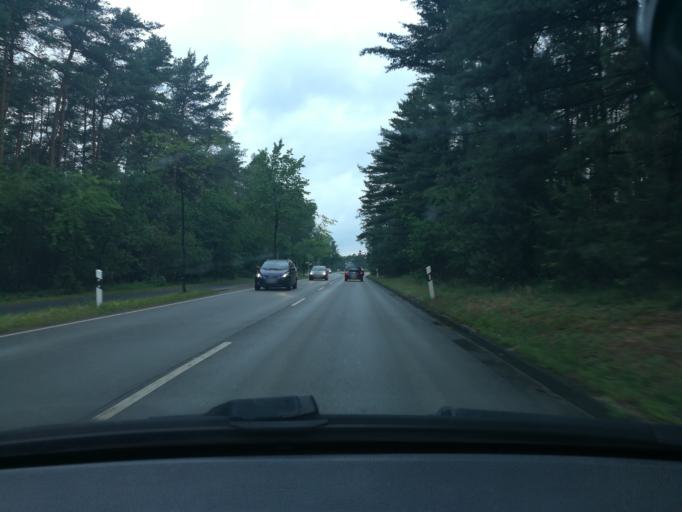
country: DE
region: North Rhine-Westphalia
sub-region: Regierungsbezirk Detmold
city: Oerlinghausen
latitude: 51.9391
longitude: 8.6476
